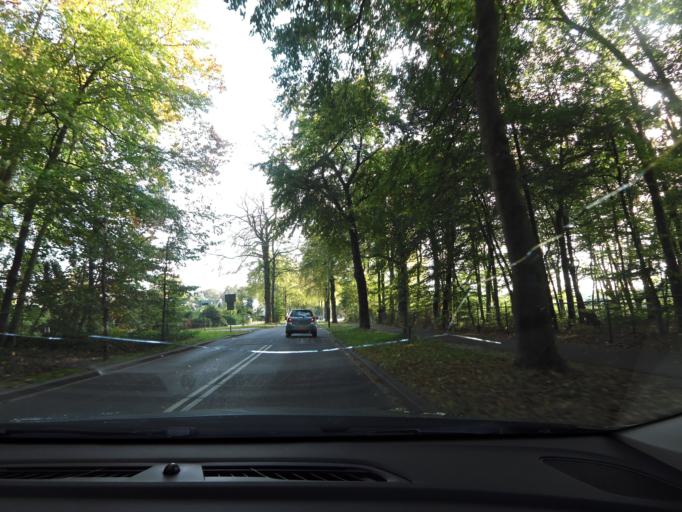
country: NL
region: Utrecht
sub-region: Gemeente Rhenen
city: Rhenen
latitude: 51.9700
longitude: 5.5655
